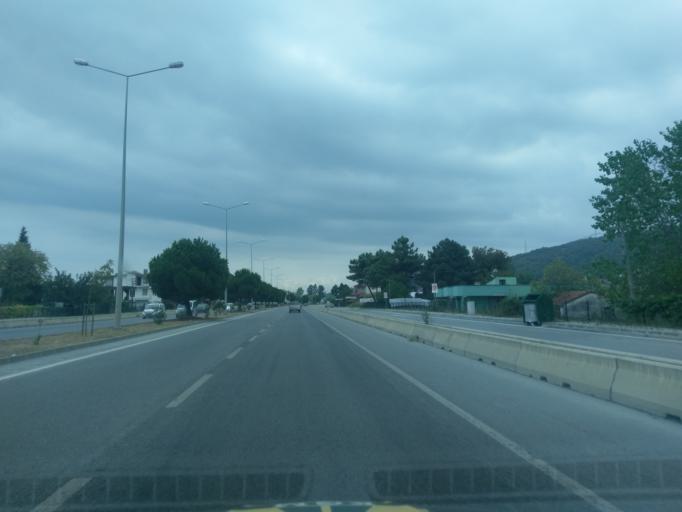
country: TR
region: Samsun
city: Taflan
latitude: 41.3973
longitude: 36.1959
